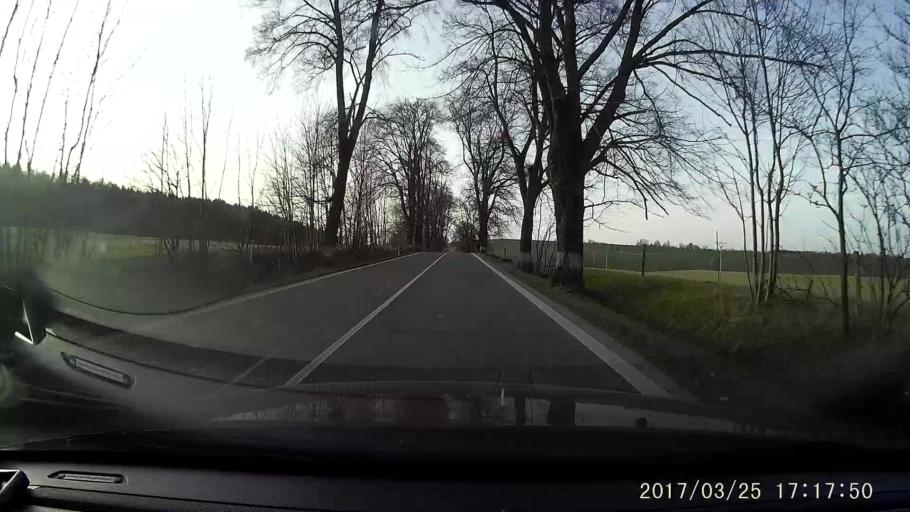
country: CZ
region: Liberecky
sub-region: Okres Liberec
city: Frydlant
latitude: 50.9708
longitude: 15.0921
